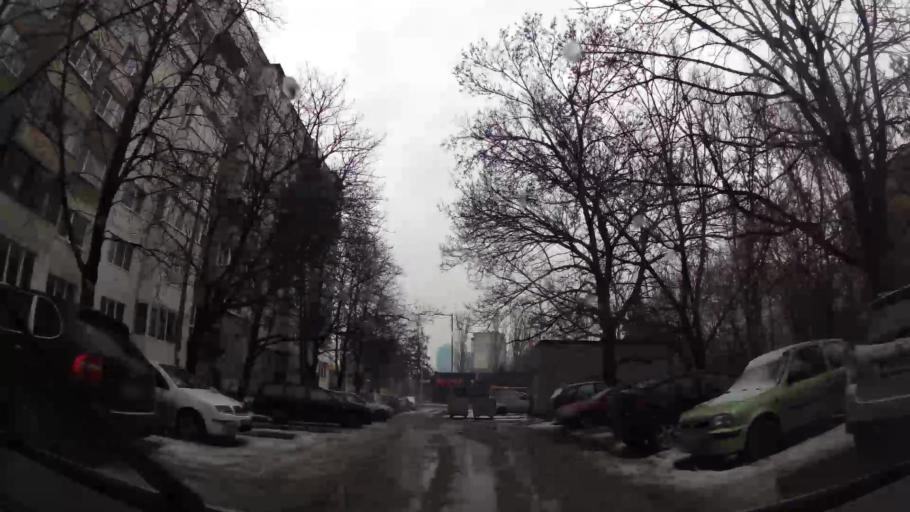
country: BG
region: Sofia-Capital
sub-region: Stolichna Obshtina
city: Sofia
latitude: 42.6618
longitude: 23.2964
